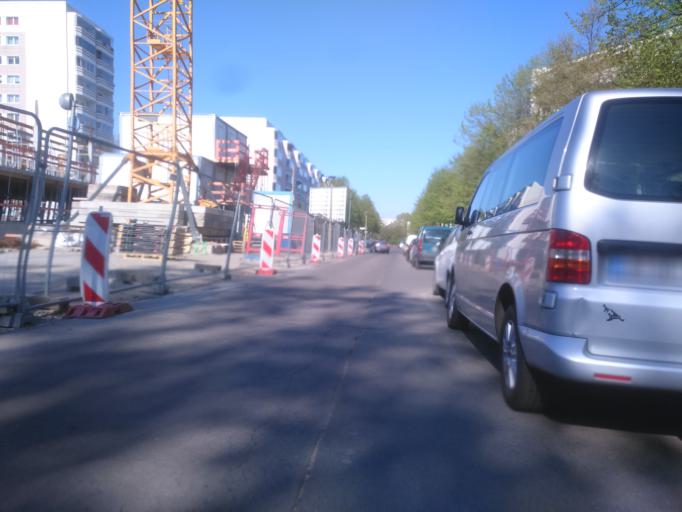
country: DE
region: Berlin
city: Neu-Hohenschoenhausen
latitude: 52.5602
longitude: 13.5104
